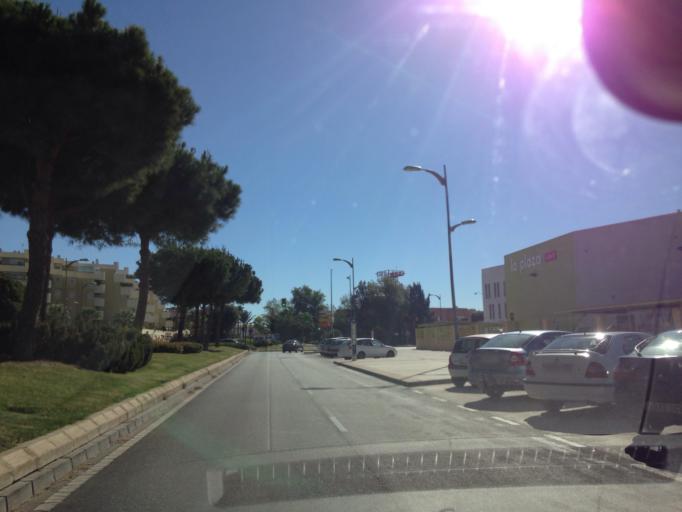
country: ES
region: Andalusia
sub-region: Provincia de Malaga
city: Malaga
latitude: 36.6877
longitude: -4.4537
